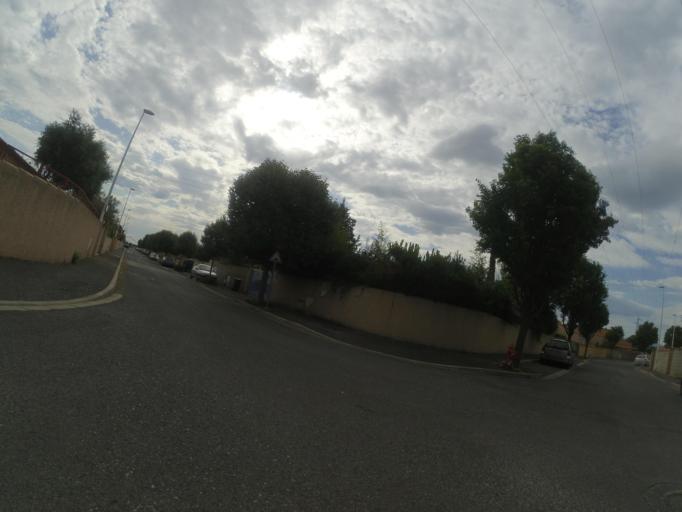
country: FR
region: Languedoc-Roussillon
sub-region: Departement des Pyrenees-Orientales
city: Toulouges
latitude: 42.6752
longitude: 2.8460
